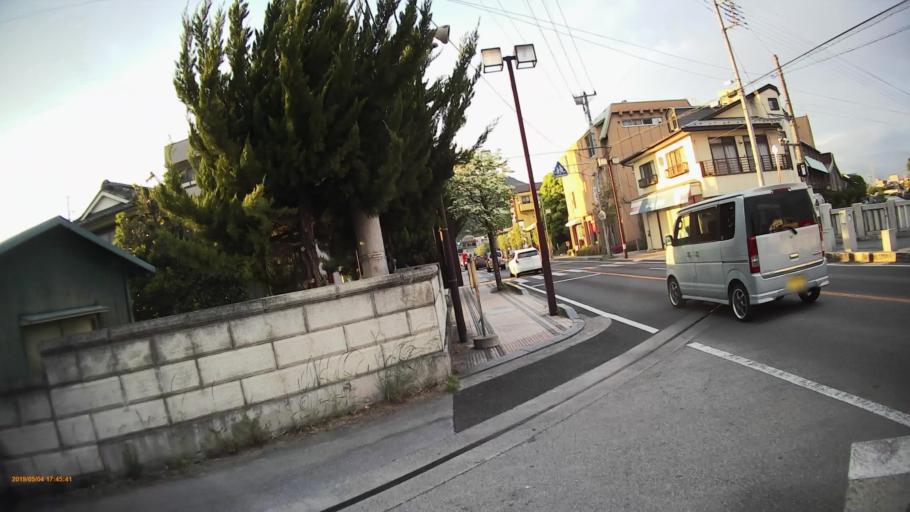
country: JP
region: Yamanashi
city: Isawa
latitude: 35.6537
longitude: 138.6355
